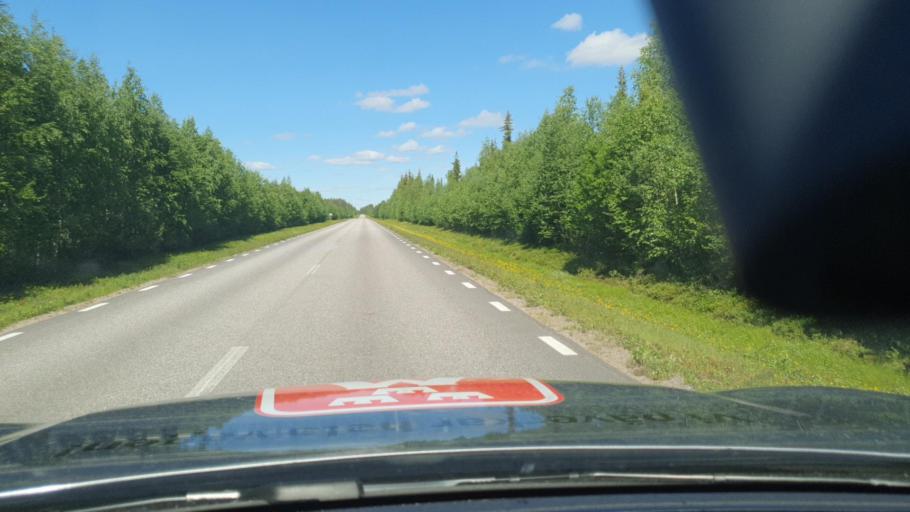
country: SE
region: Norrbotten
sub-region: Overkalix Kommun
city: OEverkalix
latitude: 66.9729
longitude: 22.6403
